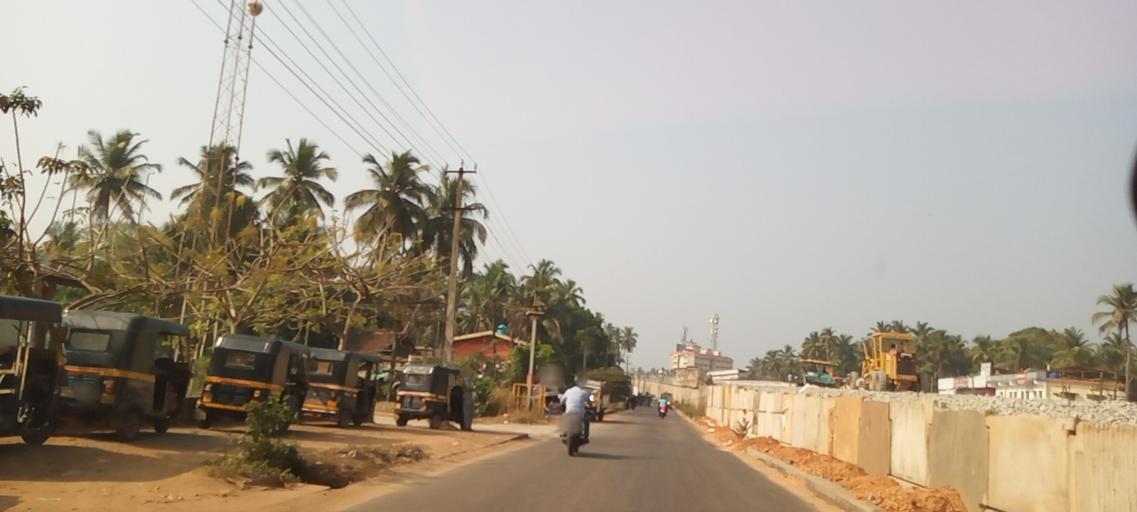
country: IN
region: Karnataka
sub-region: Udupi
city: Coondapoor
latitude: 13.6272
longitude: 74.6952
